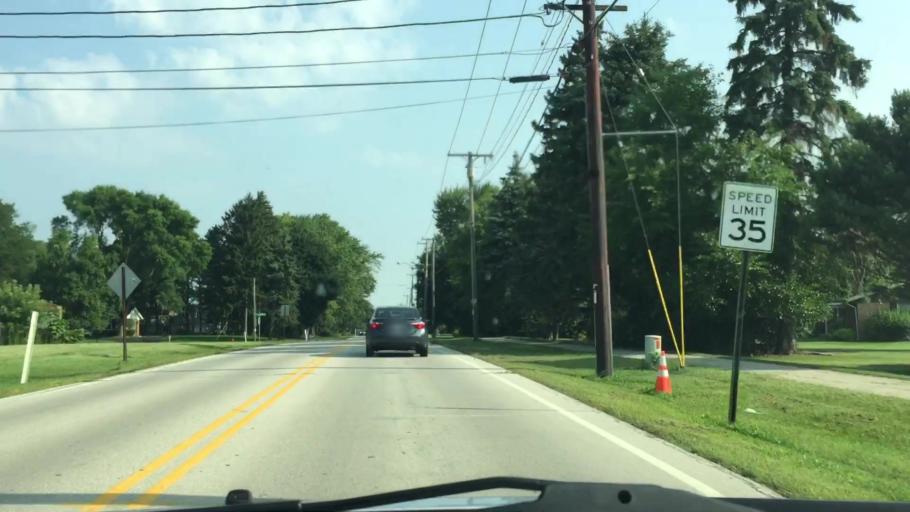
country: US
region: Wisconsin
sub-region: Waukesha County
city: Brookfield
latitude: 43.0508
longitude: -88.1462
